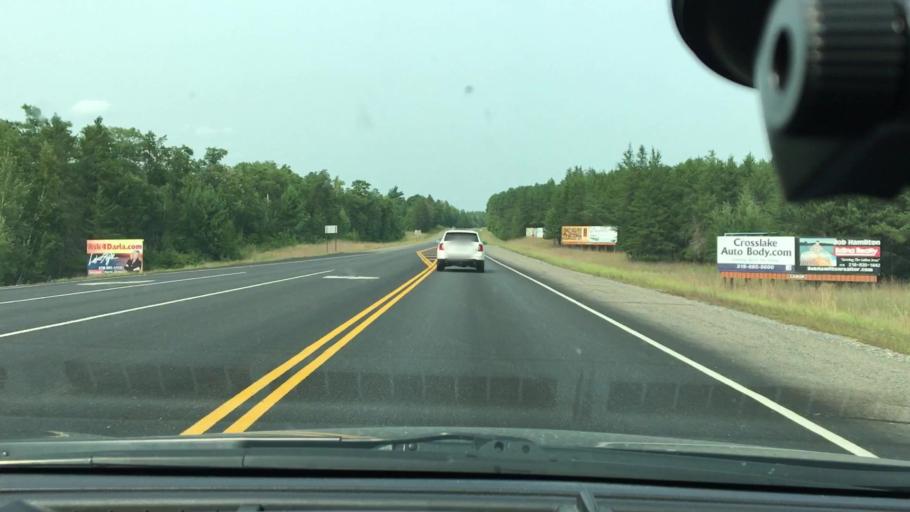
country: US
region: Minnesota
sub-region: Crow Wing County
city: Cross Lake
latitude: 46.6177
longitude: -94.1318
